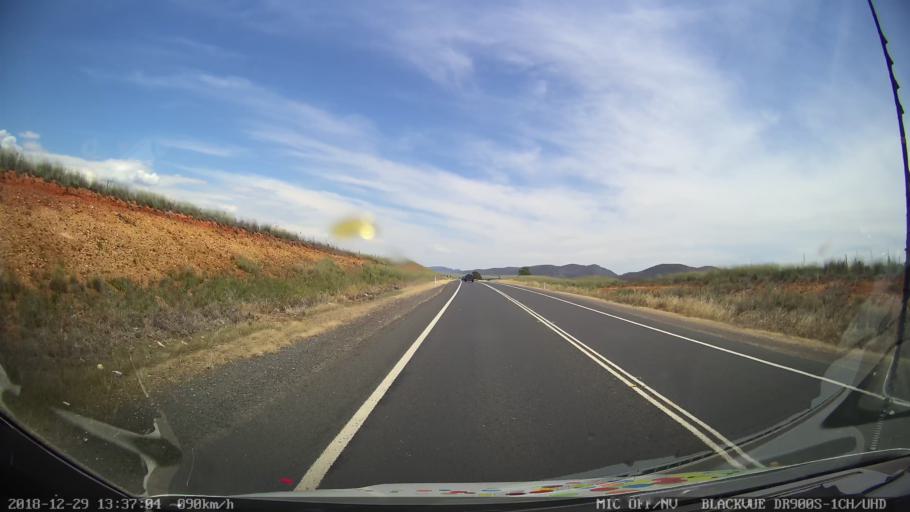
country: AU
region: New South Wales
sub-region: Cooma-Monaro
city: Cooma
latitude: -35.9785
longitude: 149.1374
